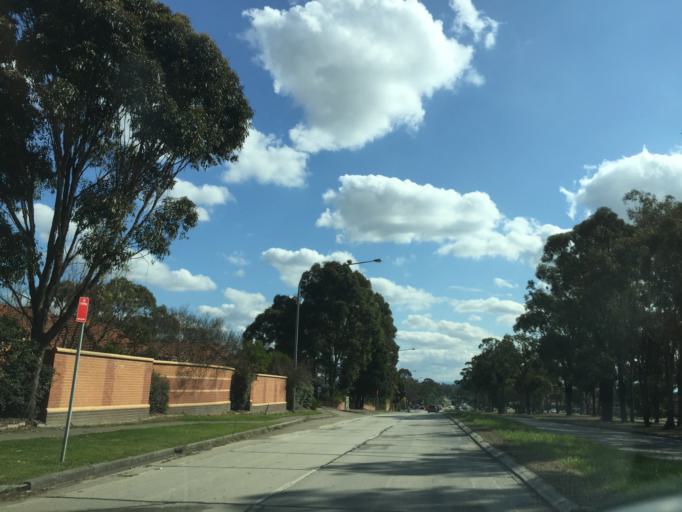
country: AU
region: New South Wales
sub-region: Blacktown
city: Quakers Hill
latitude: -33.7489
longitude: 150.8823
